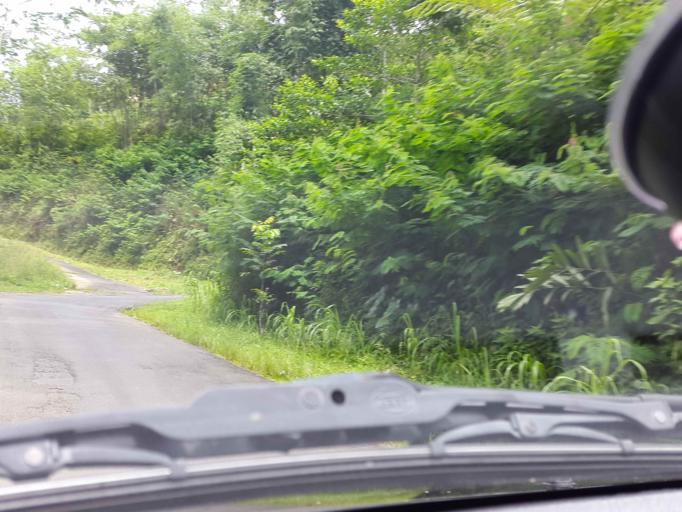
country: ID
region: Central Java
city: Wonosobo
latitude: -7.3261
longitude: 109.8533
